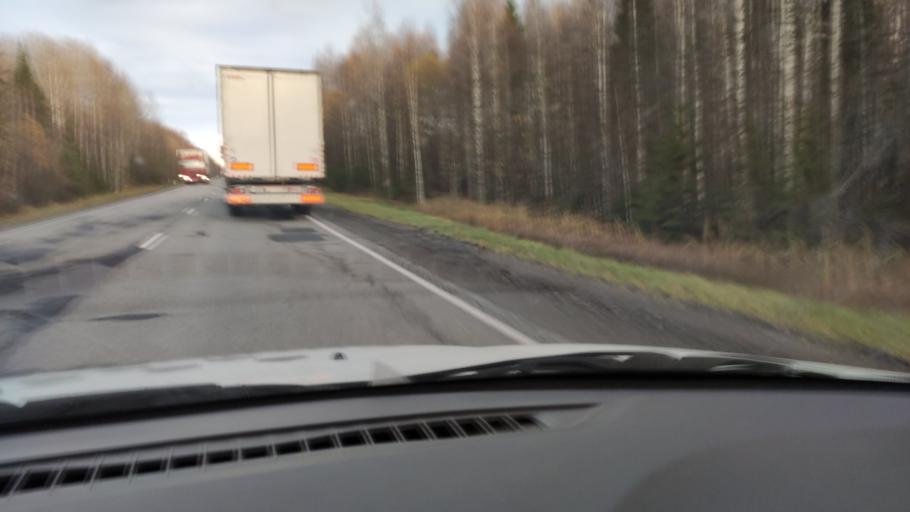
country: RU
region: Kirov
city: Chernaya Kholunitsa
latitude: 58.7712
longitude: 51.9531
